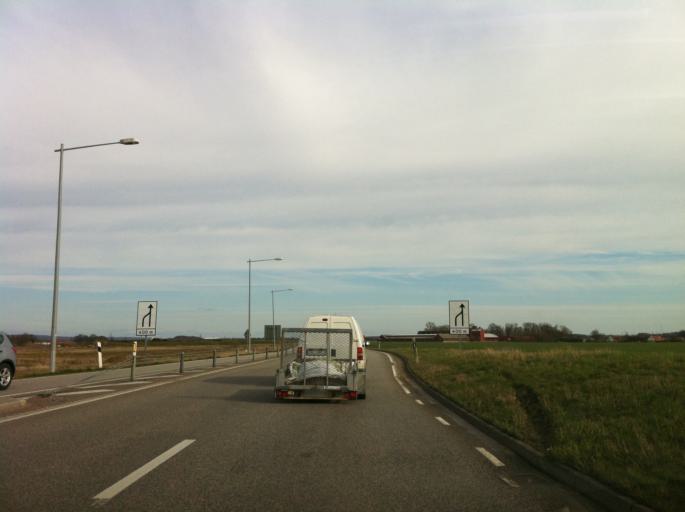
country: SE
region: Skane
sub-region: Helsingborg
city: Hyllinge
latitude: 56.0965
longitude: 12.8574
